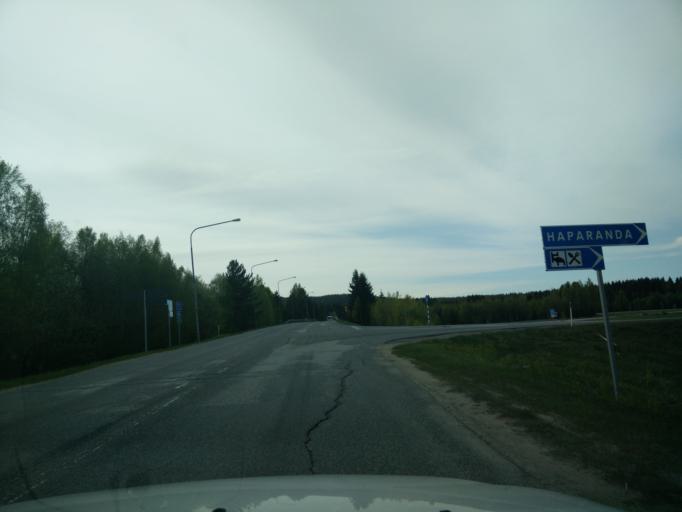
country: SE
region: Vaesternorrland
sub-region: OErnskoeldsviks Kommun
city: Bjasta
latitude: 63.2048
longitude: 18.4869
